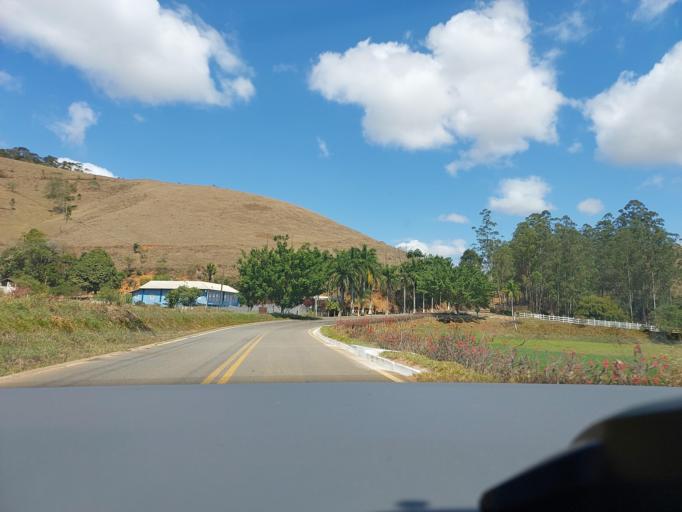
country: BR
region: Minas Gerais
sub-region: Muriae
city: Muriae
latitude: -21.0660
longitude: -42.5043
